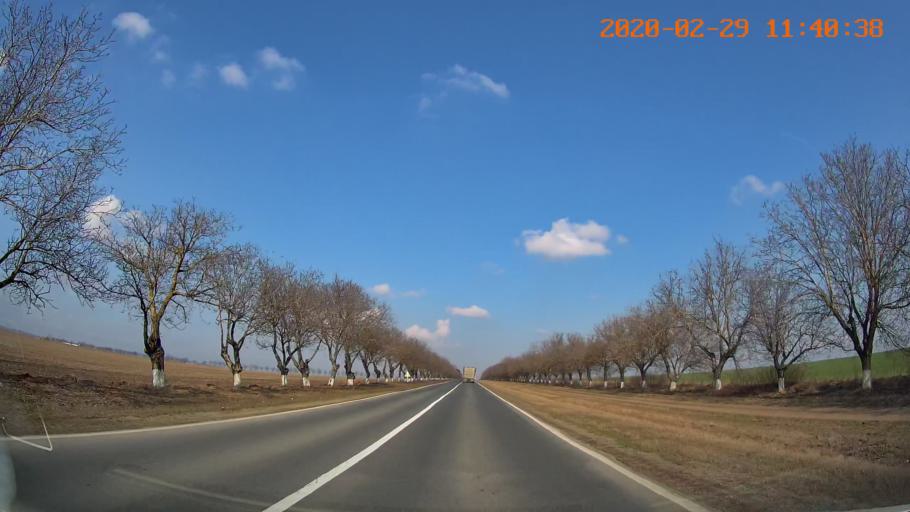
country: MD
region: Rezina
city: Saharna
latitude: 47.6592
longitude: 29.0195
